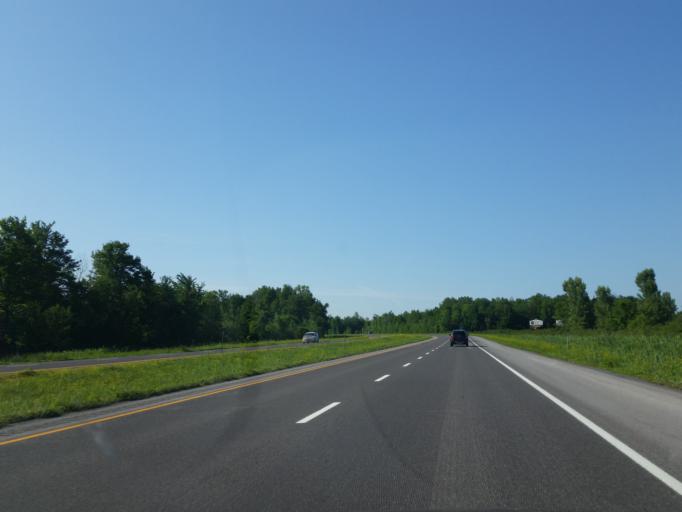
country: CA
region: Quebec
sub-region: Monteregie
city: Napierville
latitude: 45.2180
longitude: -73.4774
